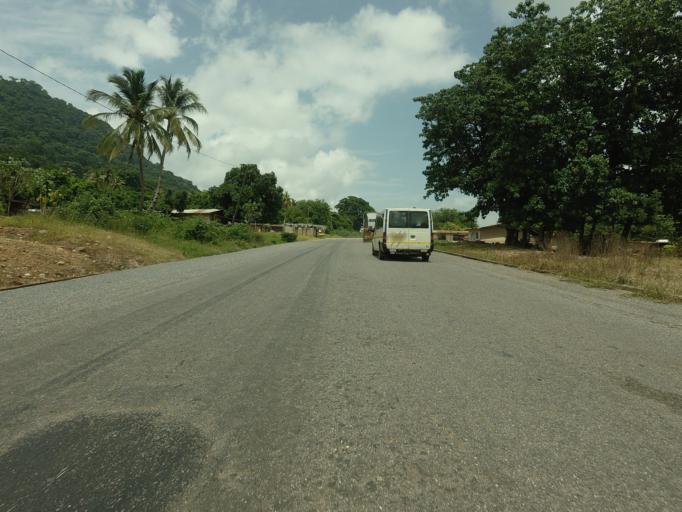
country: GH
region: Volta
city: Kpandu
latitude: 6.7953
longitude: 0.3715
